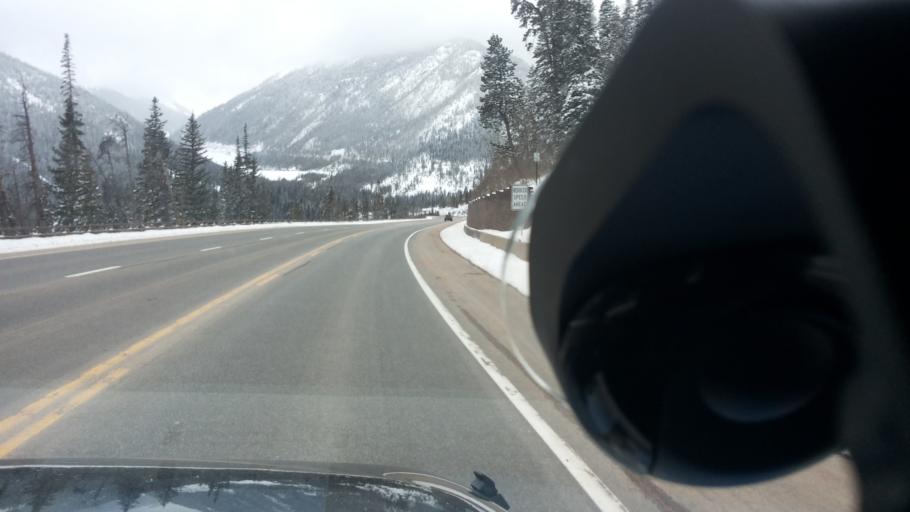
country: US
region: Colorado
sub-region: Clear Creek County
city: Georgetown
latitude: 39.7748
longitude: -105.8037
